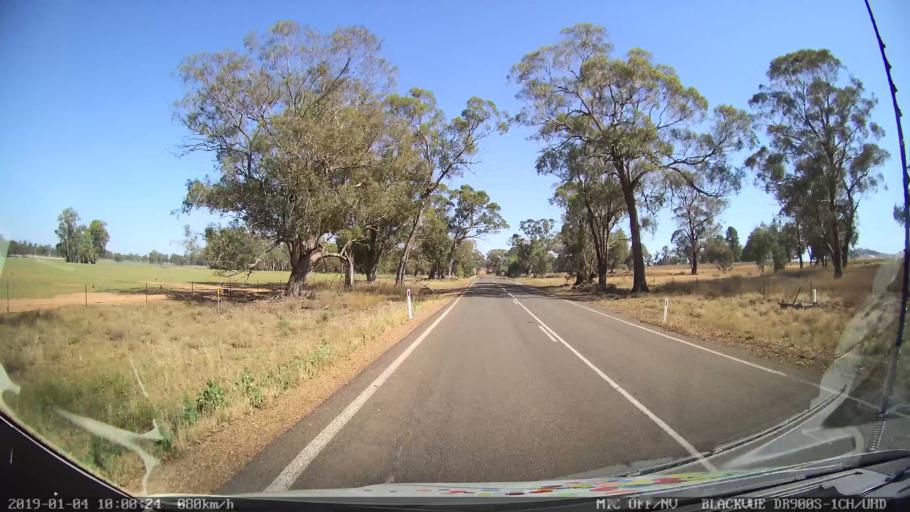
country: AU
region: New South Wales
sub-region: Cabonne
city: Canowindra
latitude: -33.4980
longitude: 148.3791
